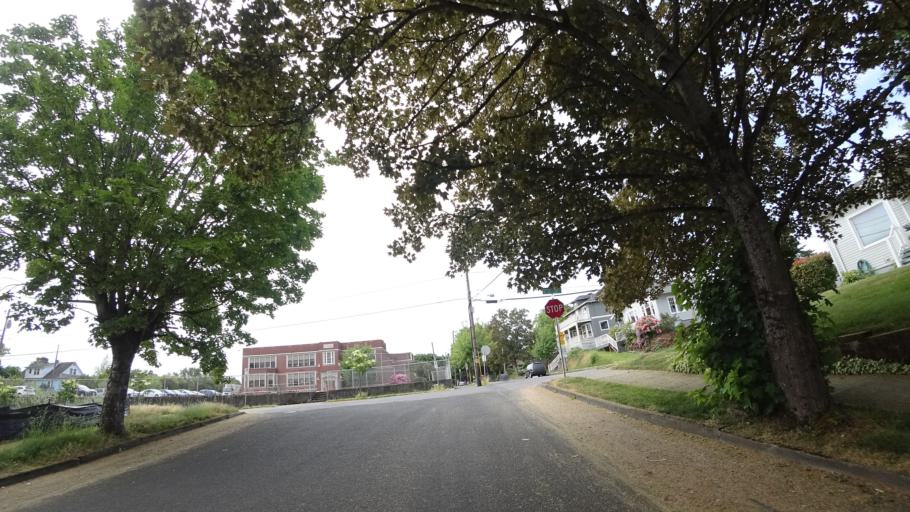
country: US
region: Oregon
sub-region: Multnomah County
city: Portland
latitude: 45.5761
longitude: -122.6536
